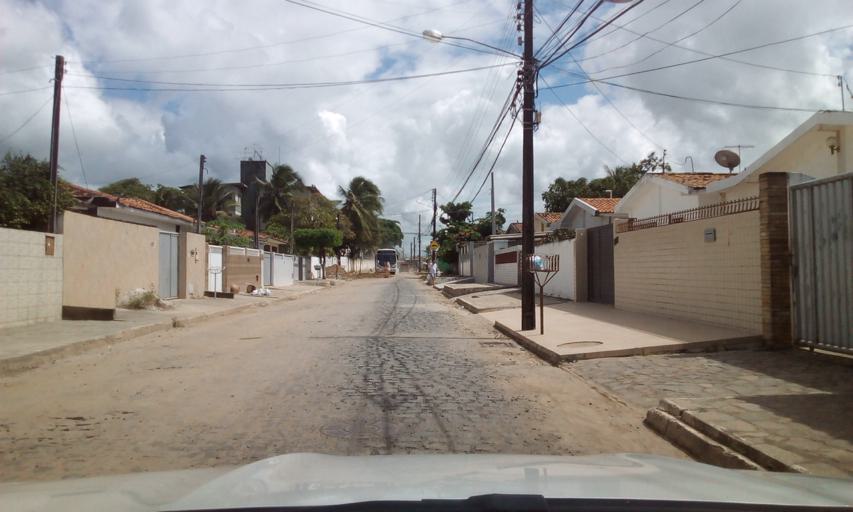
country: BR
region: Paraiba
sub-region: Joao Pessoa
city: Joao Pessoa
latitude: -7.1840
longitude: -34.8717
